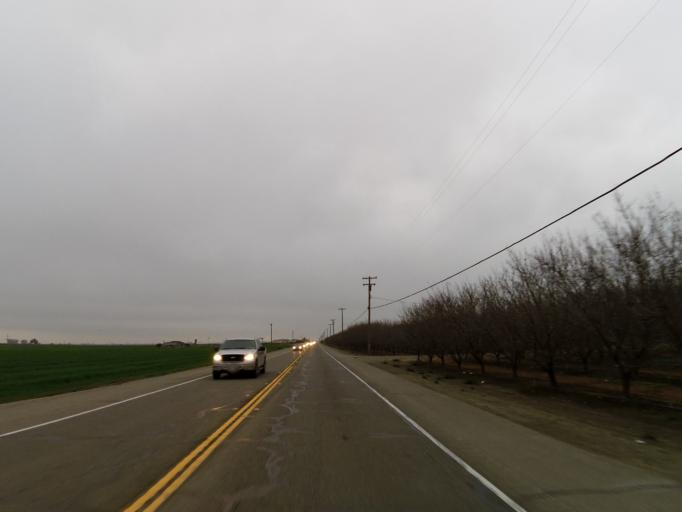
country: US
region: California
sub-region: Stanislaus County
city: Salida
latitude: 37.6379
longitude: -121.1384
